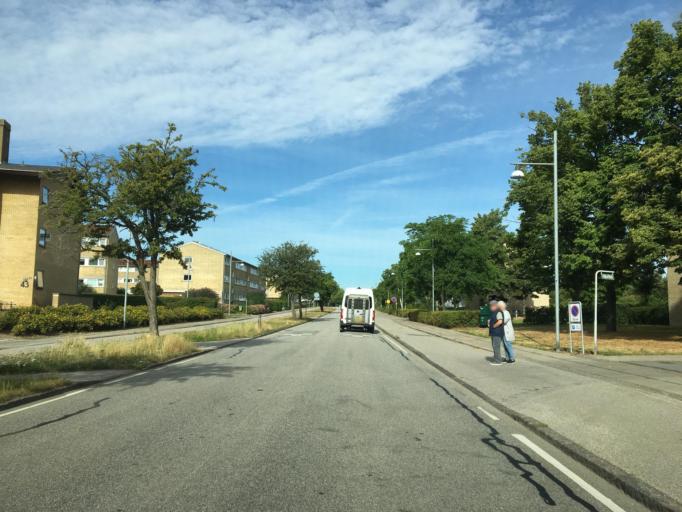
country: DK
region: Capital Region
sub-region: Glostrup Kommune
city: Glostrup
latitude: 55.6670
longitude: 12.3830
